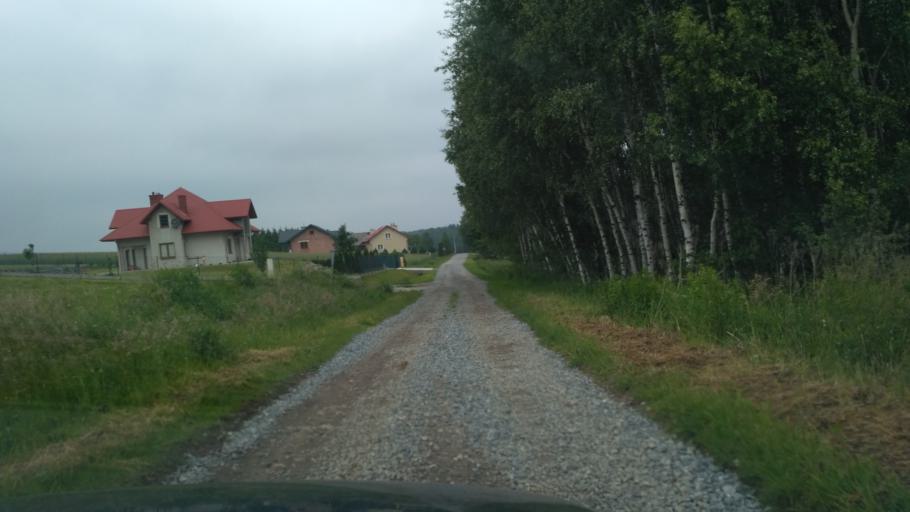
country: PL
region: Subcarpathian Voivodeship
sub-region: Powiat ropczycko-sedziszowski
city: Zagorzyce
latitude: 49.9870
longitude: 21.7059
